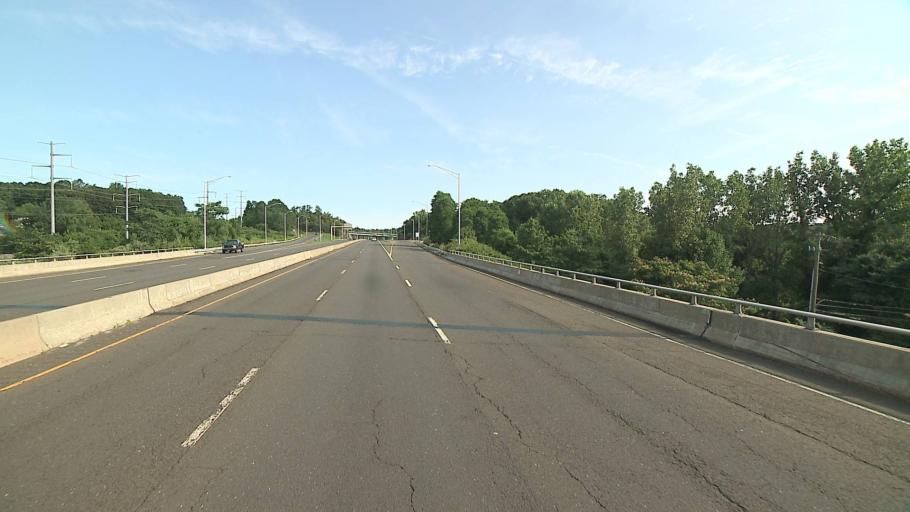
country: US
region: Connecticut
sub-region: Fairfield County
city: Norwalk
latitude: 41.1365
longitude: -73.4297
